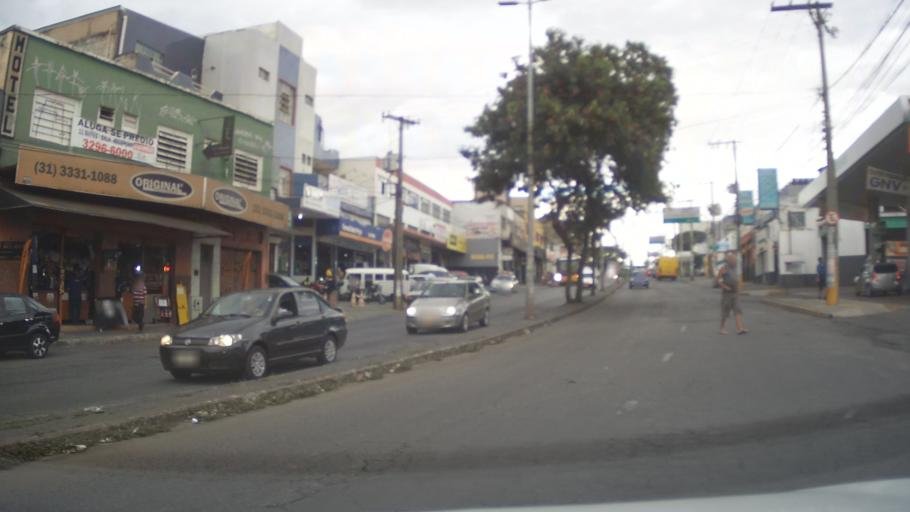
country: BR
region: Minas Gerais
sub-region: Contagem
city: Contagem
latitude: -19.9674
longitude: -44.0143
